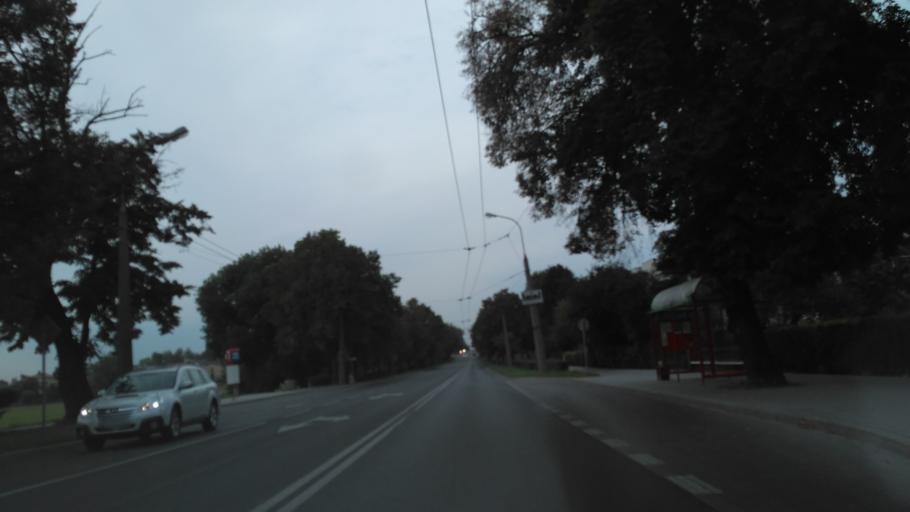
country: PL
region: Lublin Voivodeship
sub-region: Powiat lubelski
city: Lublin
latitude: 51.2271
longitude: 22.6030
